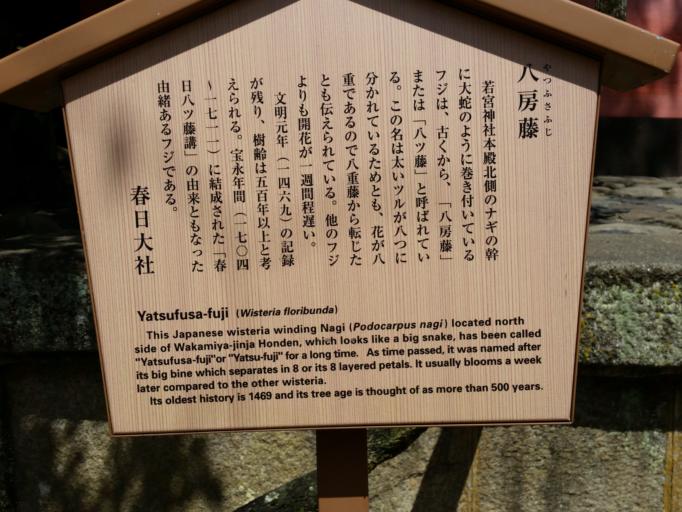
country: JP
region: Nara
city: Nara-shi
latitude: 34.6802
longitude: 135.8490
